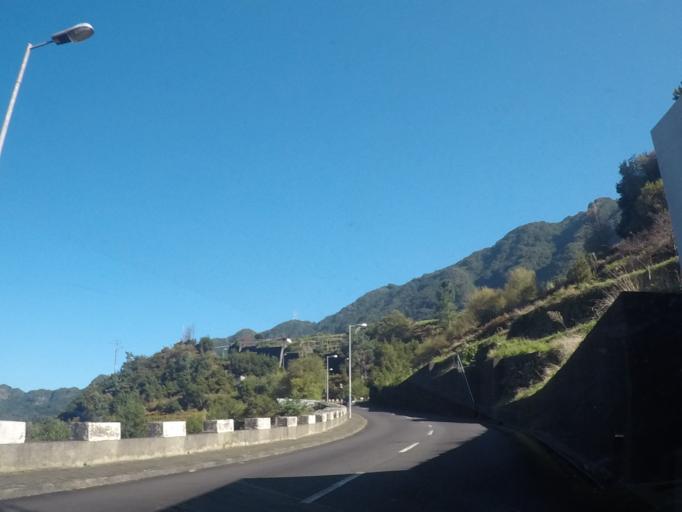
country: PT
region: Madeira
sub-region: Santana
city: Santana
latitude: 32.8007
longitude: -16.9633
